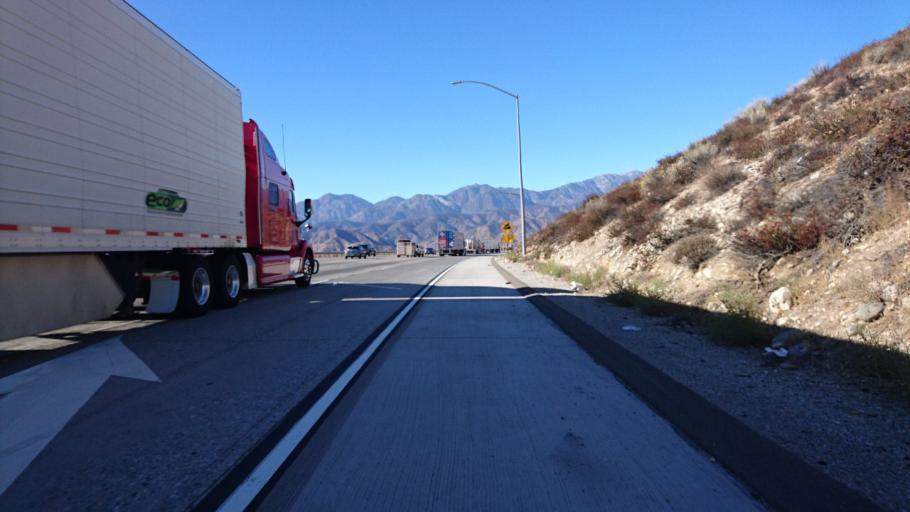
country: US
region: California
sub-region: San Bernardino County
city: Oak Hills
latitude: 34.3466
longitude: -117.4503
